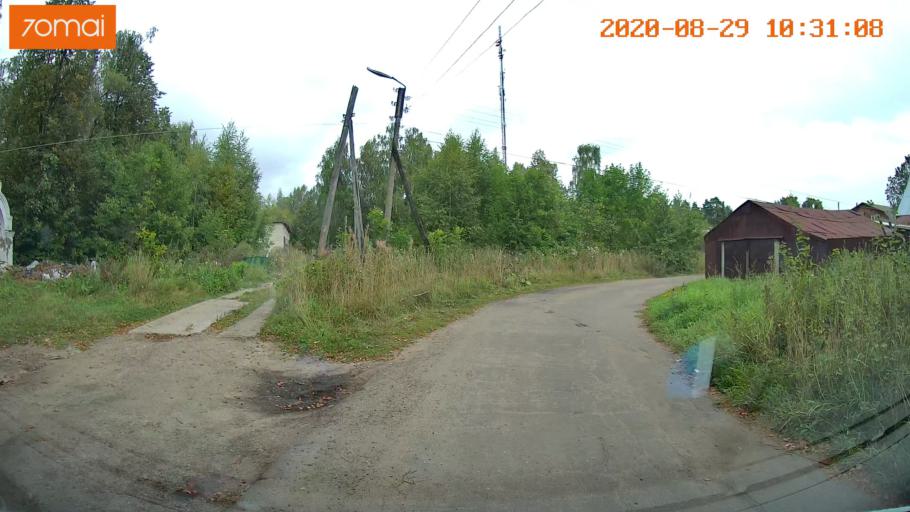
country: RU
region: Ivanovo
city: Yur'yevets
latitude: 57.3152
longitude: 43.1017
